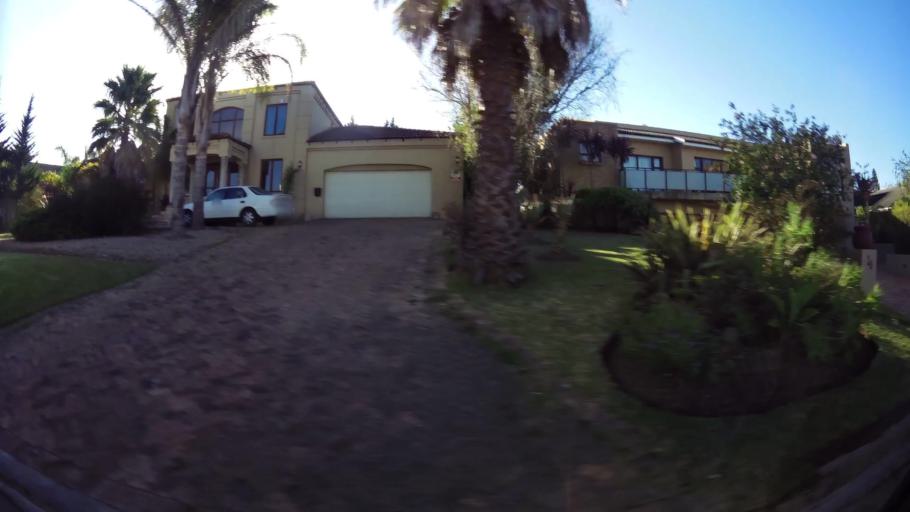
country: ZA
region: Western Cape
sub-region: Eden District Municipality
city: George
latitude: -33.9698
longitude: 22.4377
